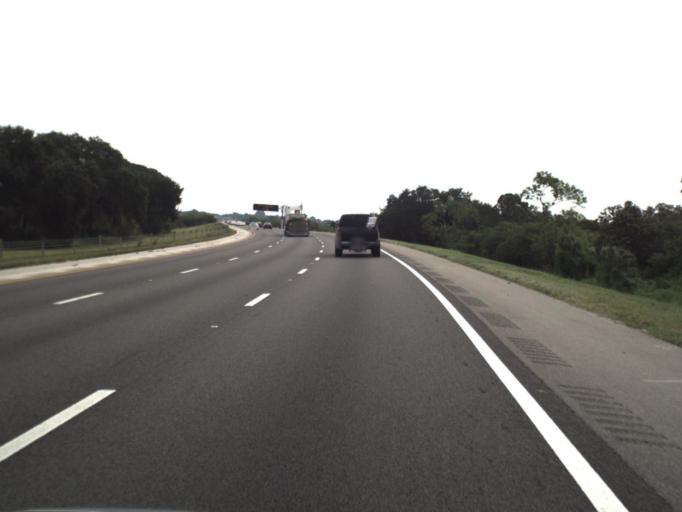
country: US
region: Florida
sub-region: Manatee County
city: Ellenton
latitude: 27.5090
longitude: -82.4981
